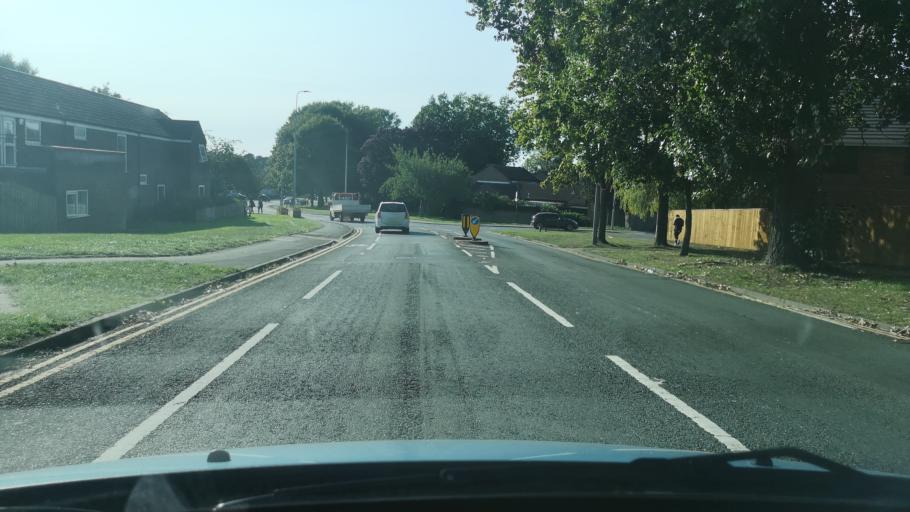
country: GB
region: England
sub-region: North Lincolnshire
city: Scunthorpe
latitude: 53.5744
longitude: -0.6761
